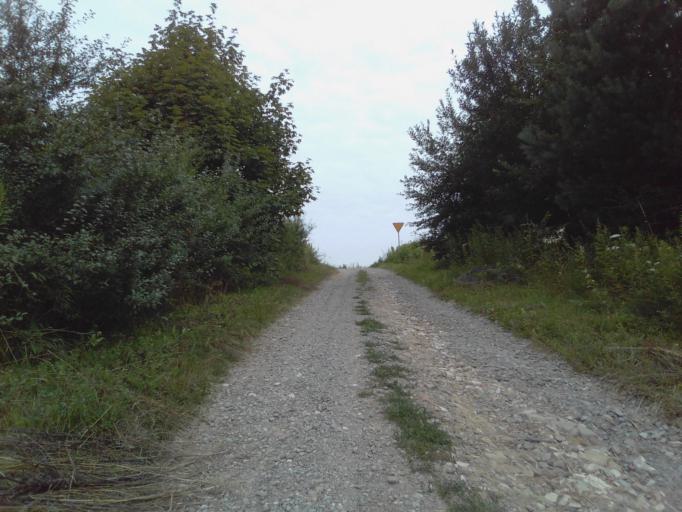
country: PL
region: Subcarpathian Voivodeship
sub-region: Powiat strzyzowski
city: Frysztak
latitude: 49.8321
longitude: 21.5506
